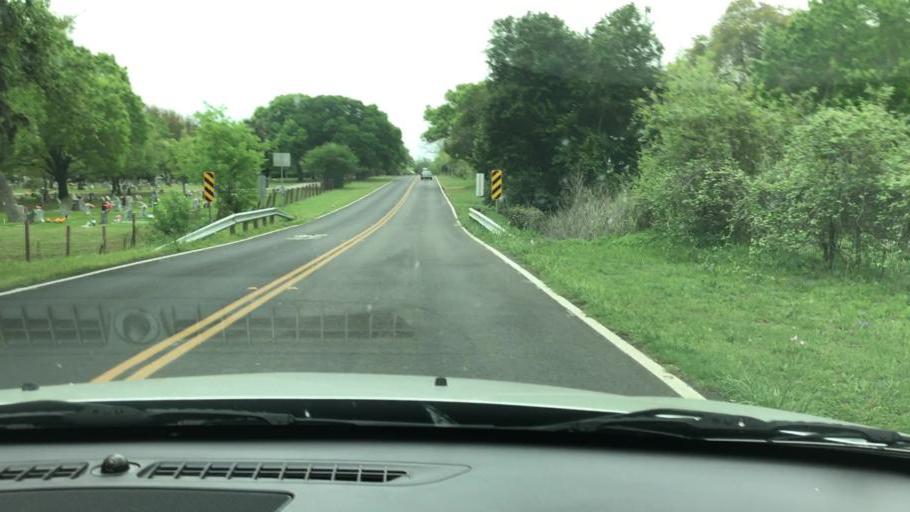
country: US
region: Texas
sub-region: Bexar County
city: San Antonio
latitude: 29.3445
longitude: -98.4717
